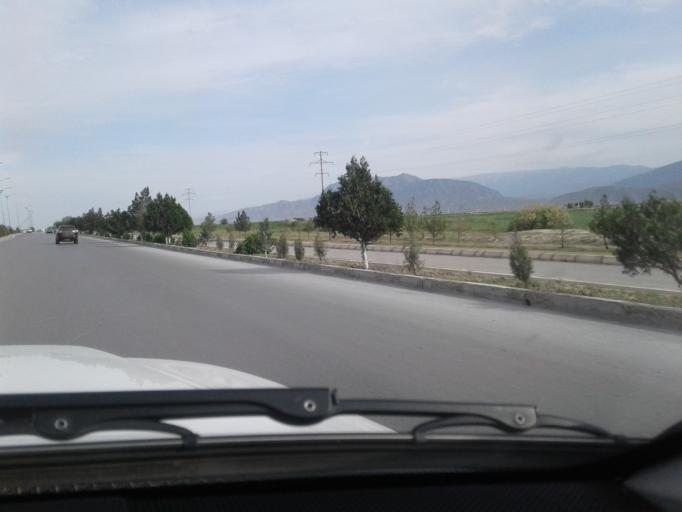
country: TM
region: Ahal
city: Abadan
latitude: 38.1517
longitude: 57.9800
